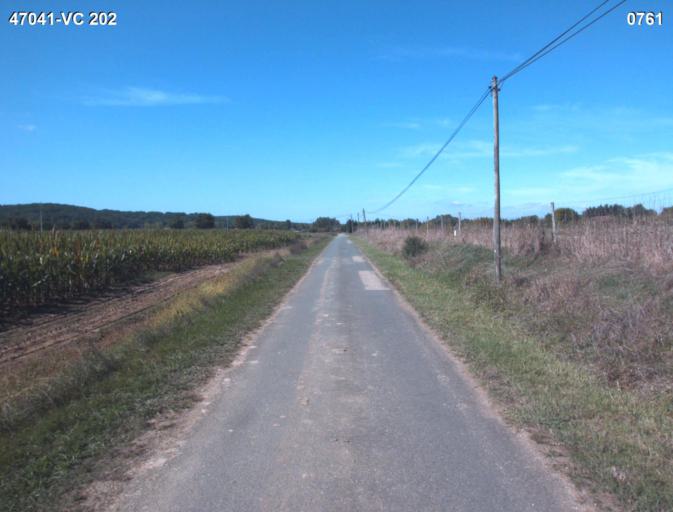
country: FR
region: Aquitaine
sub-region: Departement du Lot-et-Garonne
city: Port-Sainte-Marie
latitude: 44.2161
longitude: 0.4018
